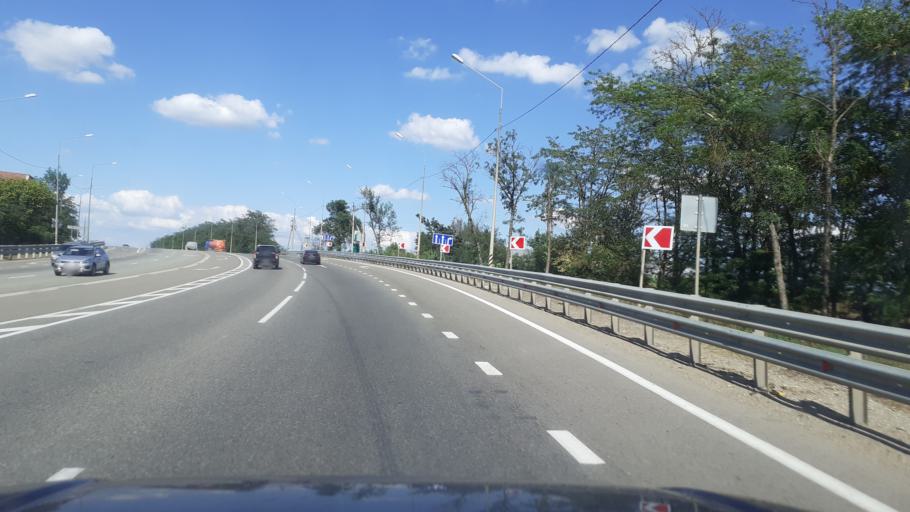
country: RU
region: Krasnodarskiy
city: Severskaya
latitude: 44.8378
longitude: 38.6923
